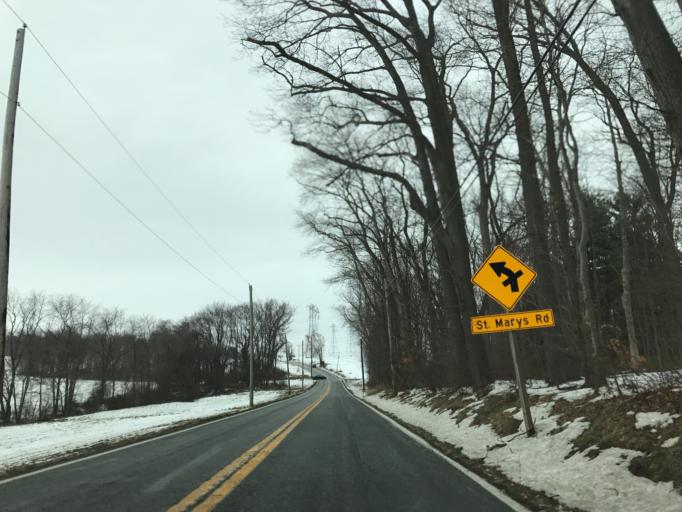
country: US
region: Pennsylvania
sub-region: York County
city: Susquehanna Trails
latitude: 39.6909
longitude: -76.4109
